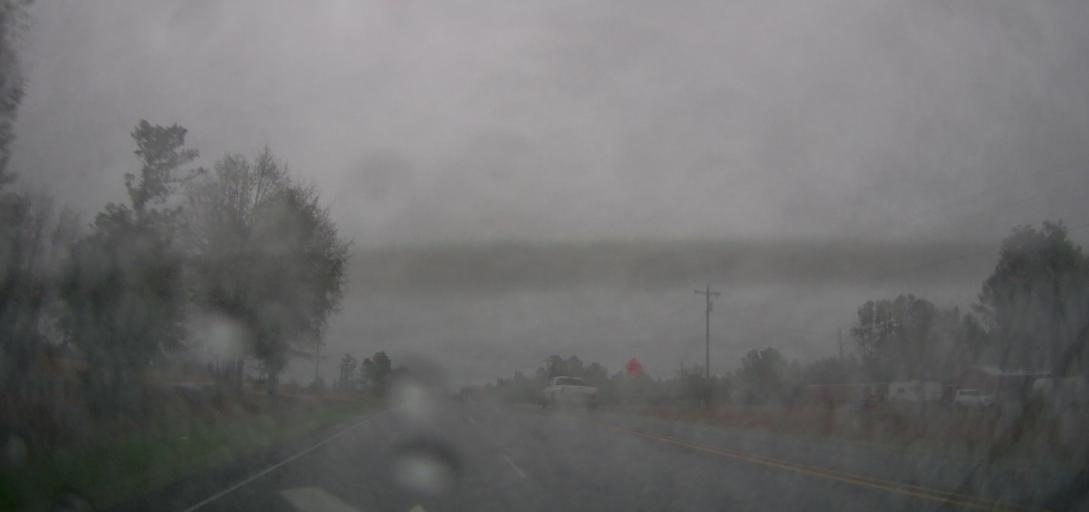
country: US
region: Alabama
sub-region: Autauga County
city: Pine Level
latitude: 32.5846
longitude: -86.6947
